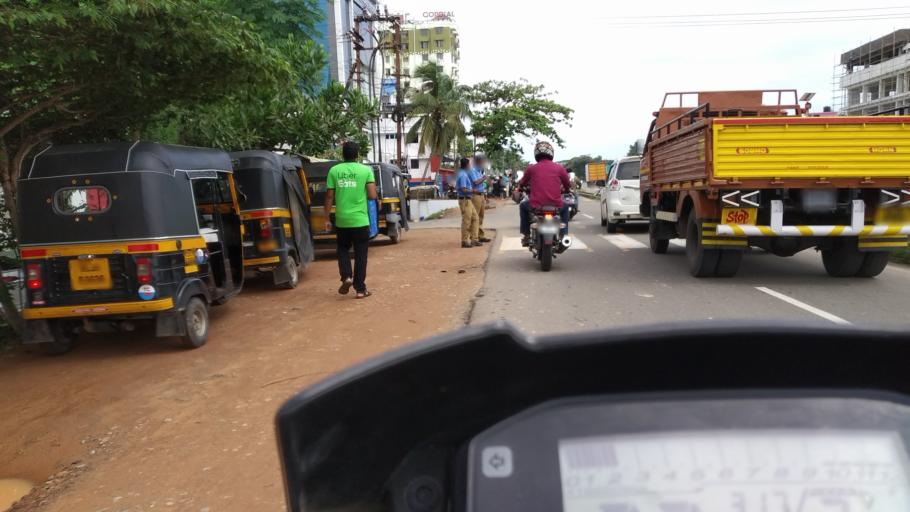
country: IN
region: Kerala
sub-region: Thiruvananthapuram
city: Thiruvananthapuram
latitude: 8.5509
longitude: 76.8771
